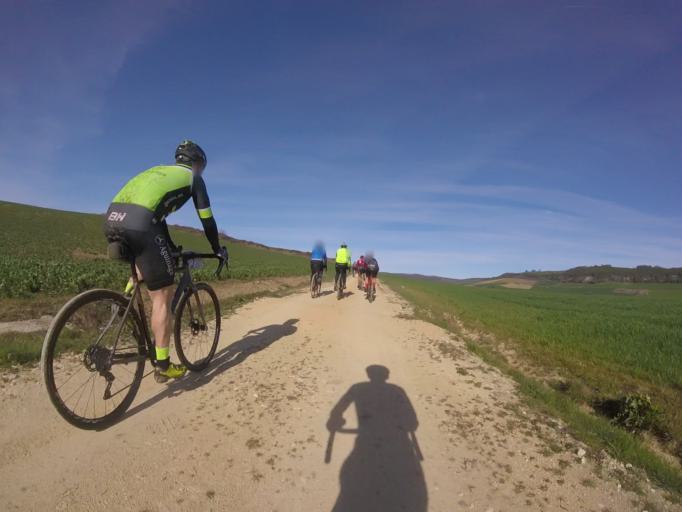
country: ES
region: Navarre
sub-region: Provincia de Navarra
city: Yerri
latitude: 42.7176
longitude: -1.9597
